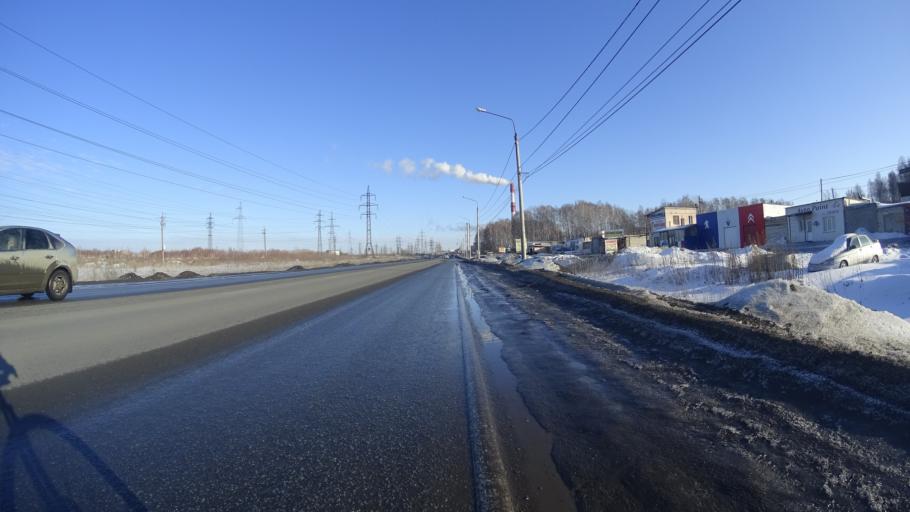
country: RU
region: Chelyabinsk
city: Roshchino
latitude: 55.2108
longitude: 61.3107
